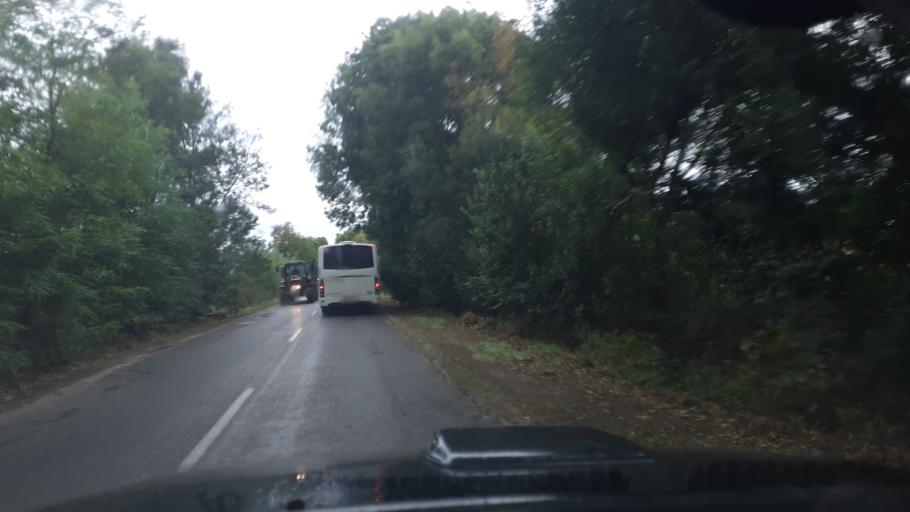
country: HU
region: Tolna
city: Dunafoldvar
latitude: 46.7759
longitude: 18.9486
